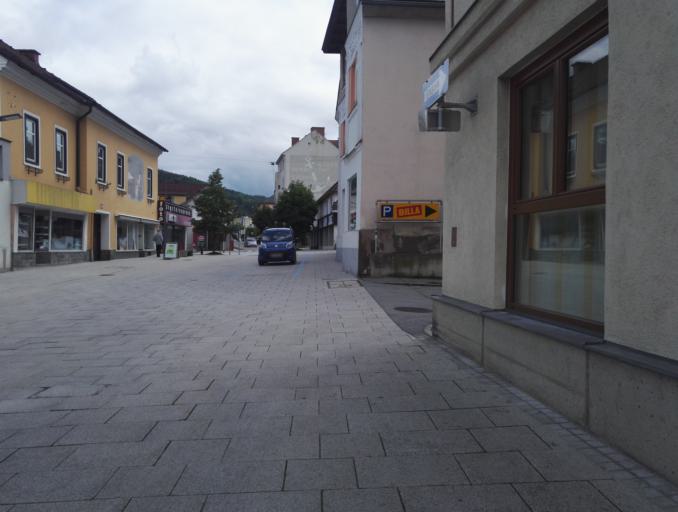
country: AT
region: Styria
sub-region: Politischer Bezirk Bruck-Muerzzuschlag
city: Muerzzuschlag
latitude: 47.6057
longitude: 15.6759
